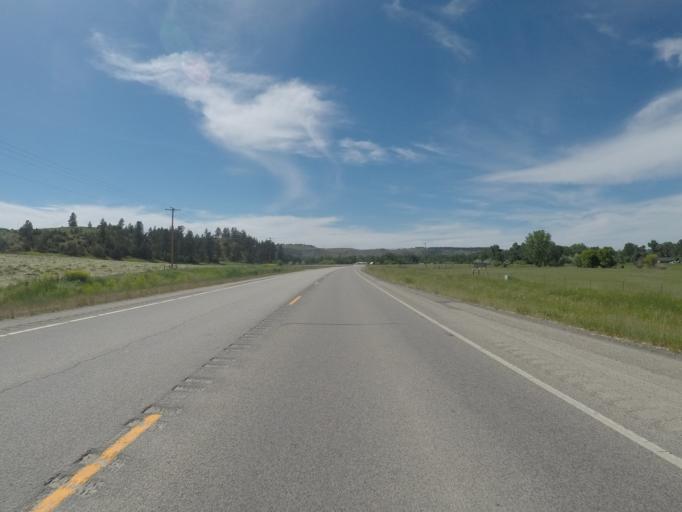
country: US
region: Montana
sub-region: Stillwater County
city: Columbus
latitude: 45.6299
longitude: -109.2677
